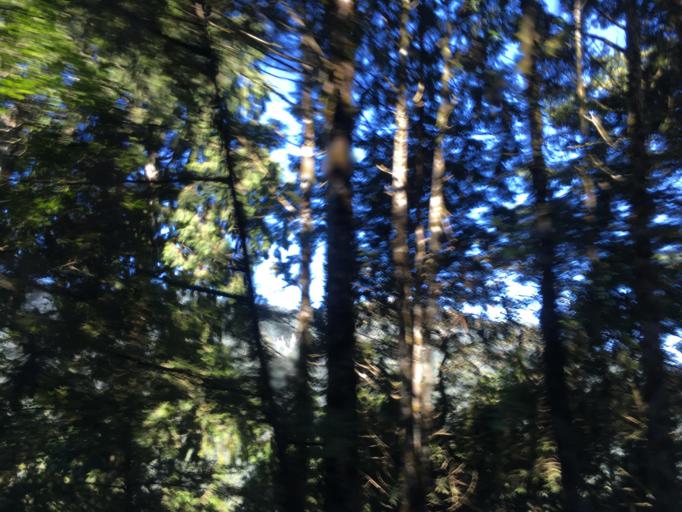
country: TW
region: Taiwan
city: Daxi
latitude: 24.6037
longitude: 121.4543
